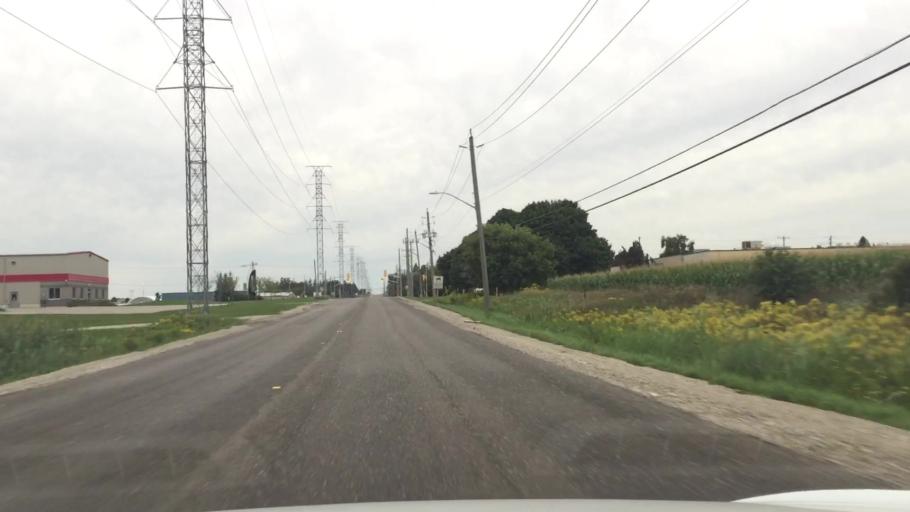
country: CA
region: Ontario
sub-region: Oxford County
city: Woodstock
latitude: 43.1238
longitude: -80.7144
